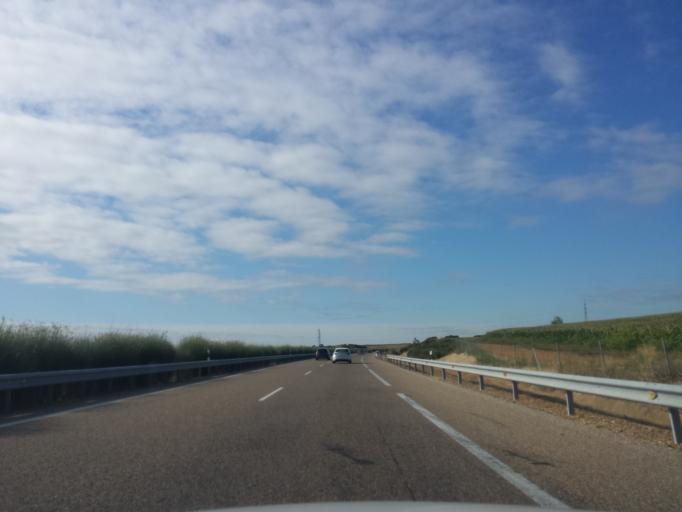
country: ES
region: Castille and Leon
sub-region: Provincia de Leon
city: Villamanan
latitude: 42.2934
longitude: -5.5896
